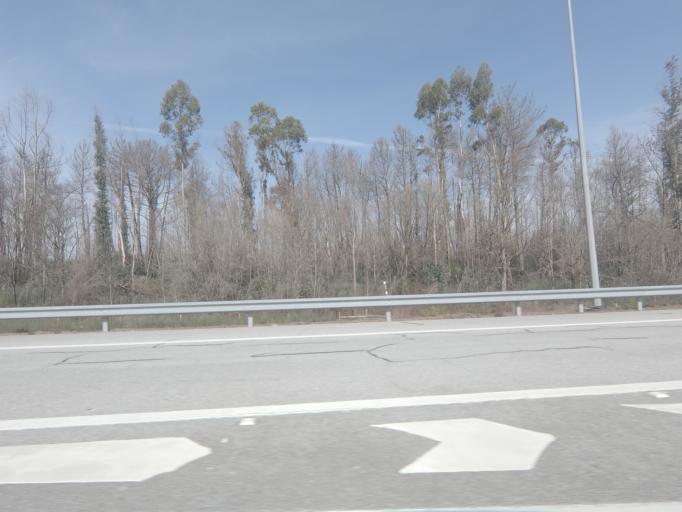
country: PT
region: Viseu
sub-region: Oliveira de Frades
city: Oliveira de Frades
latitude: 40.6838
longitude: -8.2021
